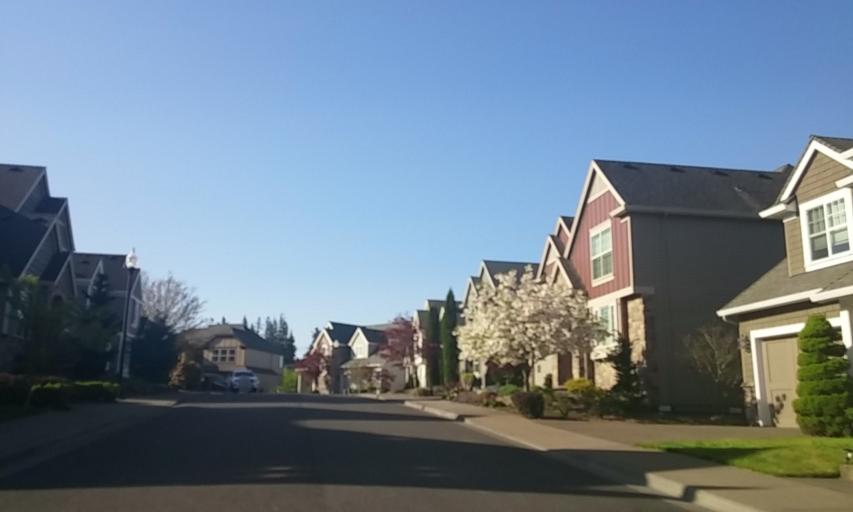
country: US
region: Oregon
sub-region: Washington County
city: Cedar Mill
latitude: 45.5474
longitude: -122.7912
